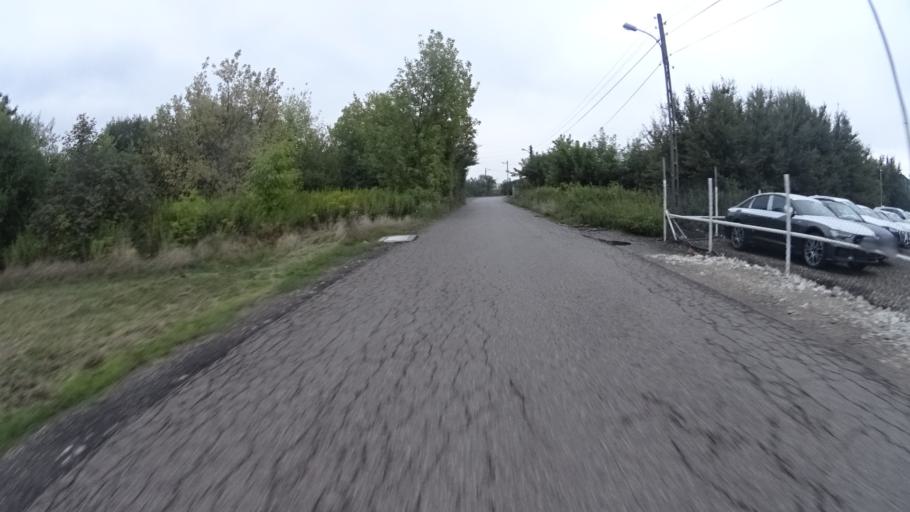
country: PL
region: Masovian Voivodeship
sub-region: Warszawa
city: Ursus
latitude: 52.2190
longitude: 20.8847
